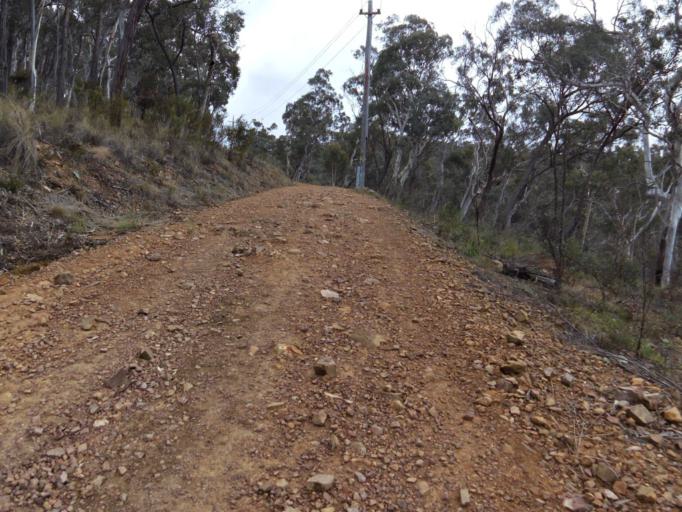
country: AU
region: Australian Capital Territory
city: Acton
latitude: -35.2711
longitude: 149.1045
